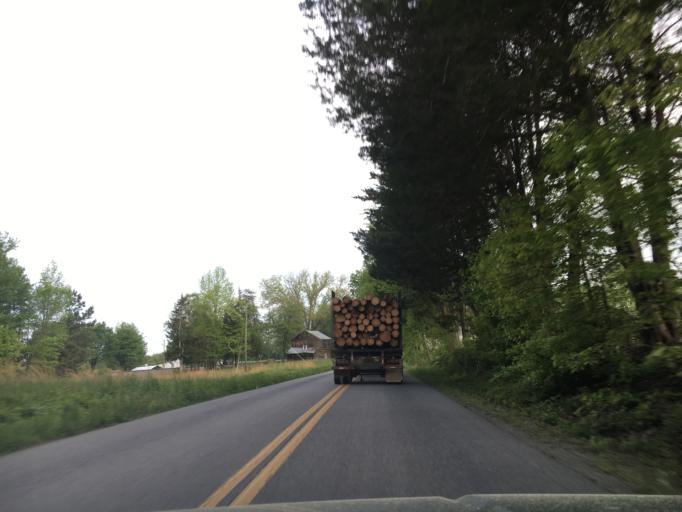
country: US
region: Virginia
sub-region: Halifax County
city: Halifax
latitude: 36.8973
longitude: -78.9063
